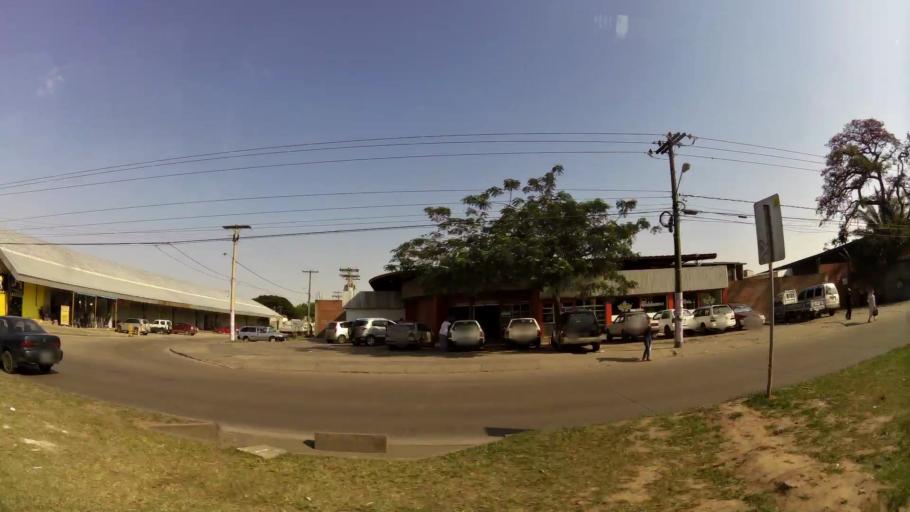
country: BO
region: Santa Cruz
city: Santa Cruz de la Sierra
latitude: -17.7855
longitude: -63.1564
